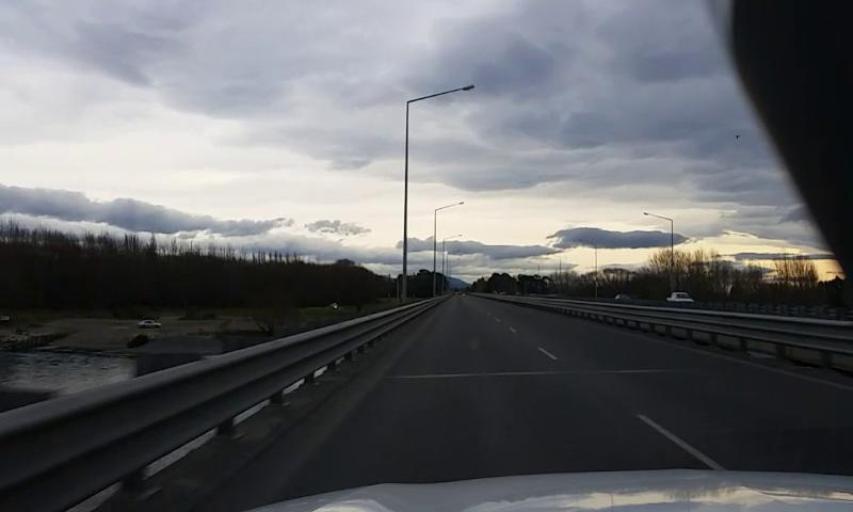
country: NZ
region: Canterbury
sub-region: Waimakariri District
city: Kaiapoi
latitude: -43.4160
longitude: 172.6468
